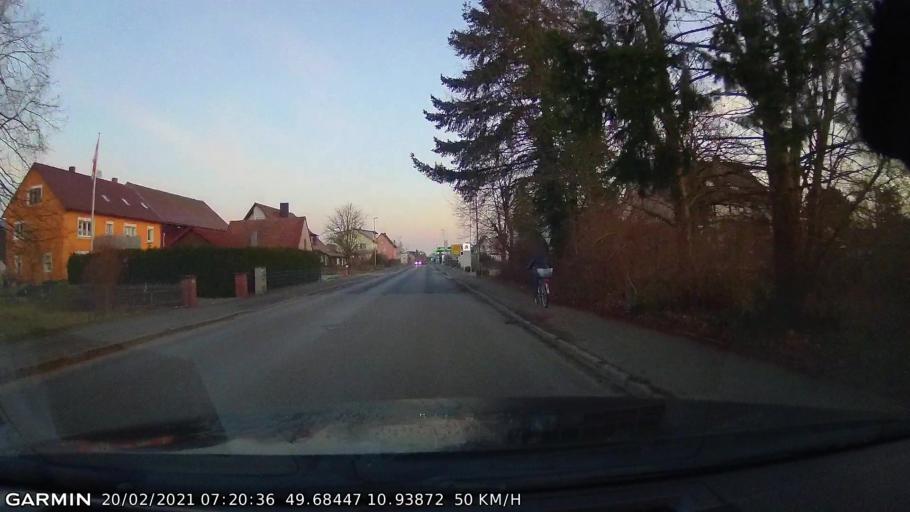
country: DE
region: Bavaria
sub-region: Regierungsbezirk Mittelfranken
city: Hemhofen
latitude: 49.6845
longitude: 10.9387
